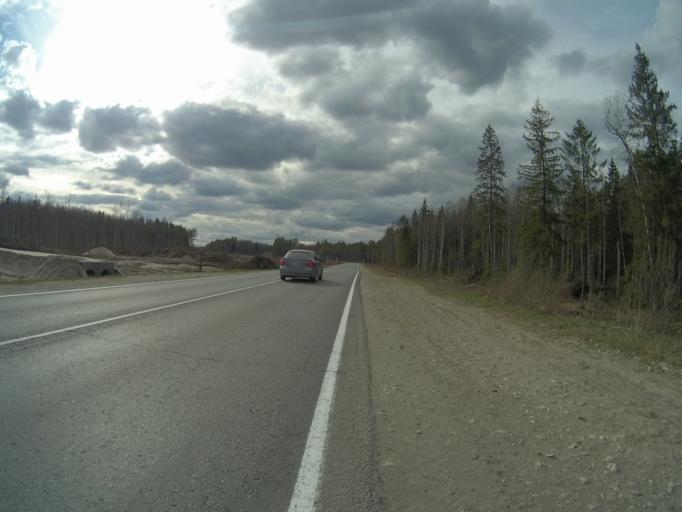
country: RU
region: Vladimir
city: Orgtrud
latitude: 56.0111
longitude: 40.6060
